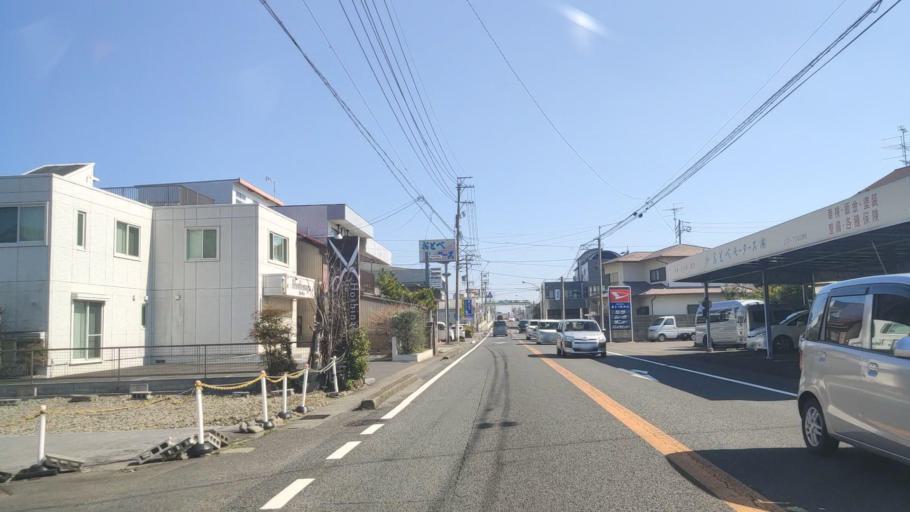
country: JP
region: Gifu
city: Gifu-shi
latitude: 35.3968
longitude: 136.7694
